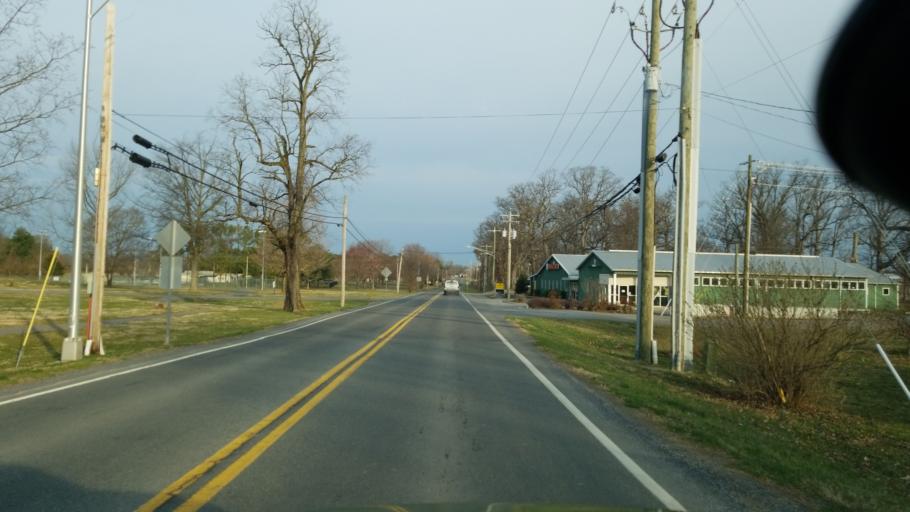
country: US
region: Virginia
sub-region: Clarke County
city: Berryville
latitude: 39.1623
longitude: -77.9977
